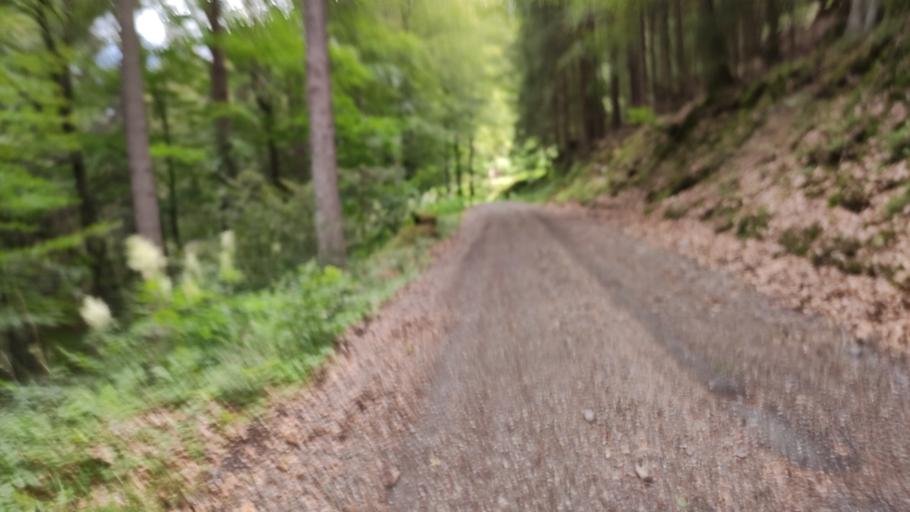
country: DE
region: Bavaria
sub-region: Upper Franconia
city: Tschirn
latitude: 50.3810
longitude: 11.4665
